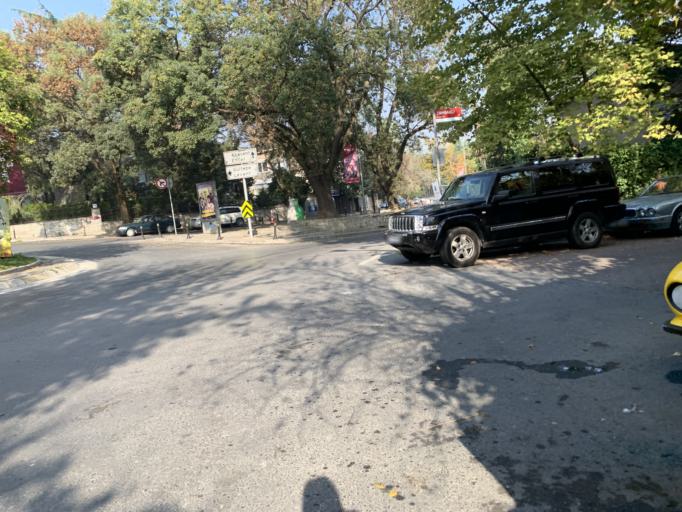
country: TR
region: Istanbul
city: Sisli
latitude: 41.0833
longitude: 29.0146
